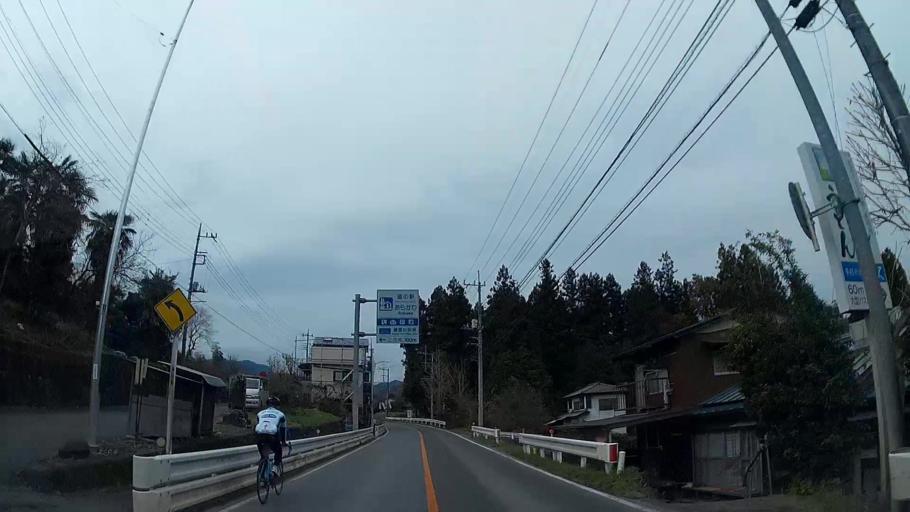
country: JP
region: Saitama
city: Chichibu
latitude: 35.9559
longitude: 139.0162
